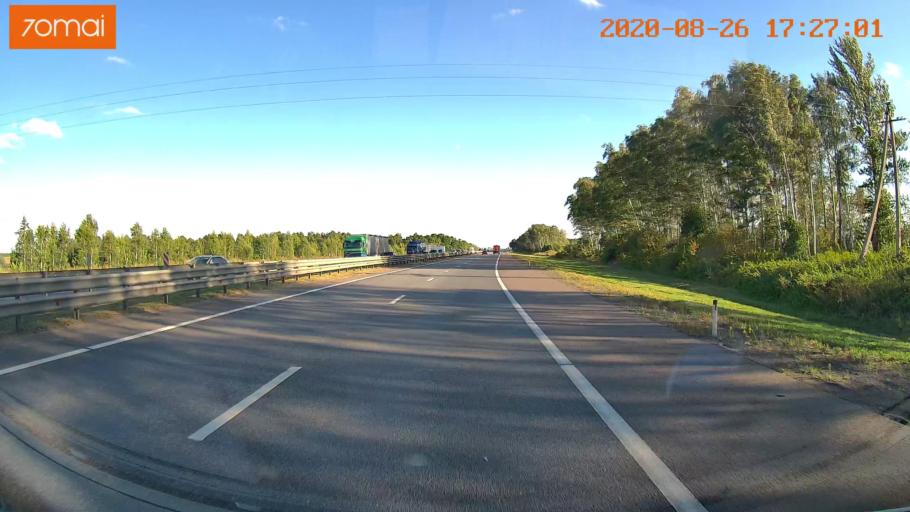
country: RU
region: Tula
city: Kazachka
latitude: 53.4786
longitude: 38.1214
